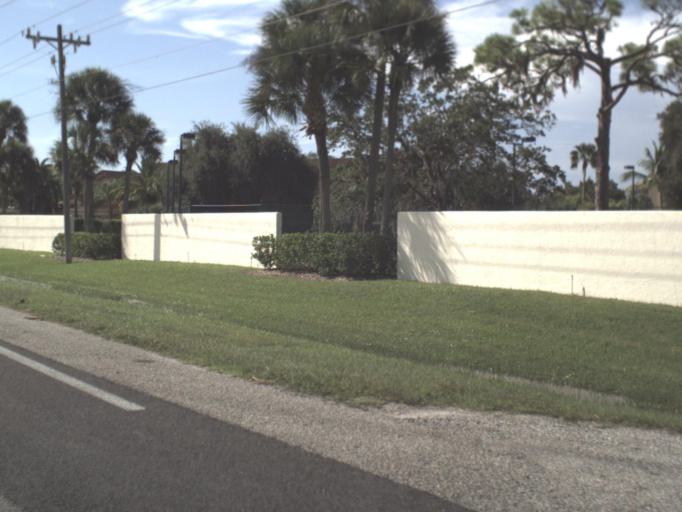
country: US
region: Florida
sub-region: Sarasota County
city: Laurel
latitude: 27.1662
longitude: -82.4762
